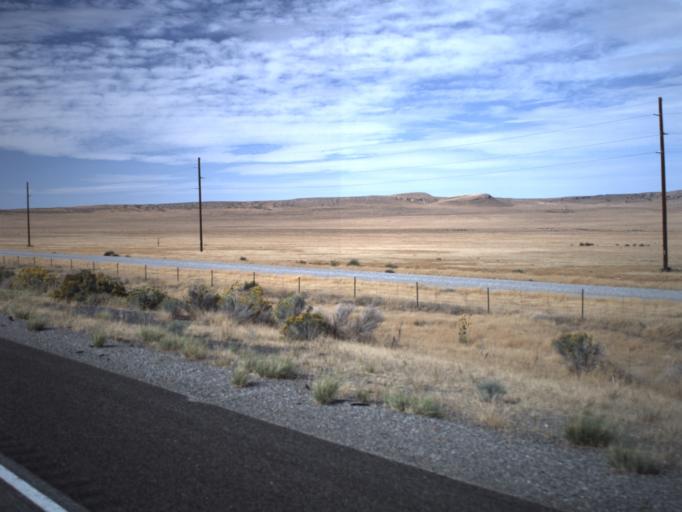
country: US
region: Utah
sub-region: Tooele County
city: Grantsville
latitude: 40.7891
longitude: -112.9575
